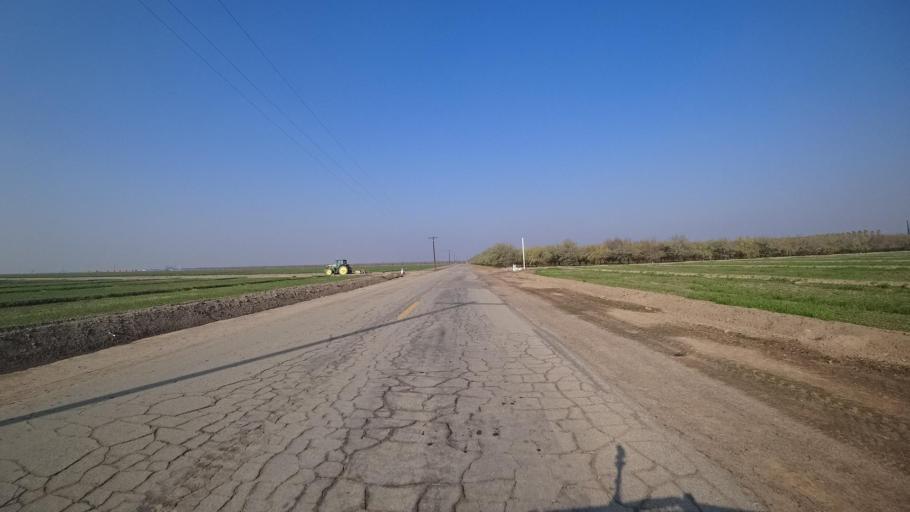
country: US
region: California
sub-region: Kern County
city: Greenfield
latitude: 35.1895
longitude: -119.0435
